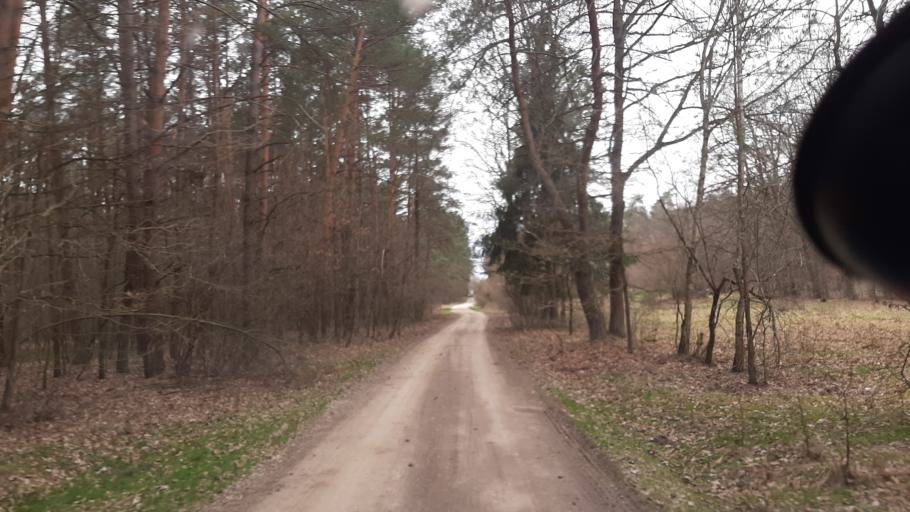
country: PL
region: Lublin Voivodeship
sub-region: Powiat lubartowski
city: Abramow
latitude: 51.4445
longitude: 22.3413
